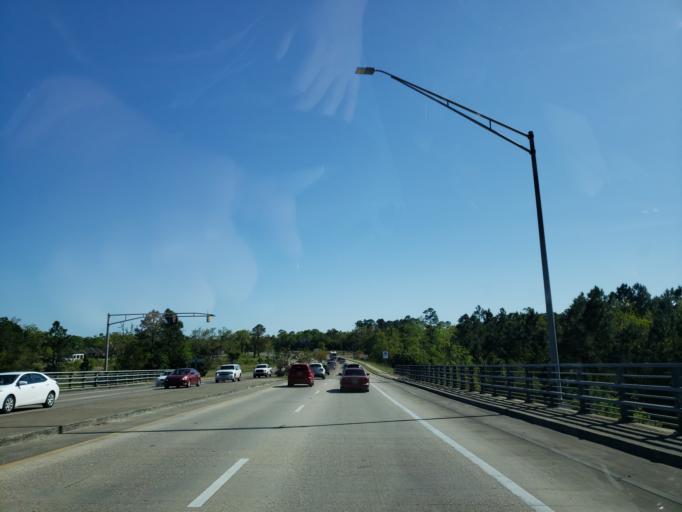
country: US
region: Mississippi
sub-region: Harrison County
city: West Gulfport
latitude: 30.4233
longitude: -89.0322
